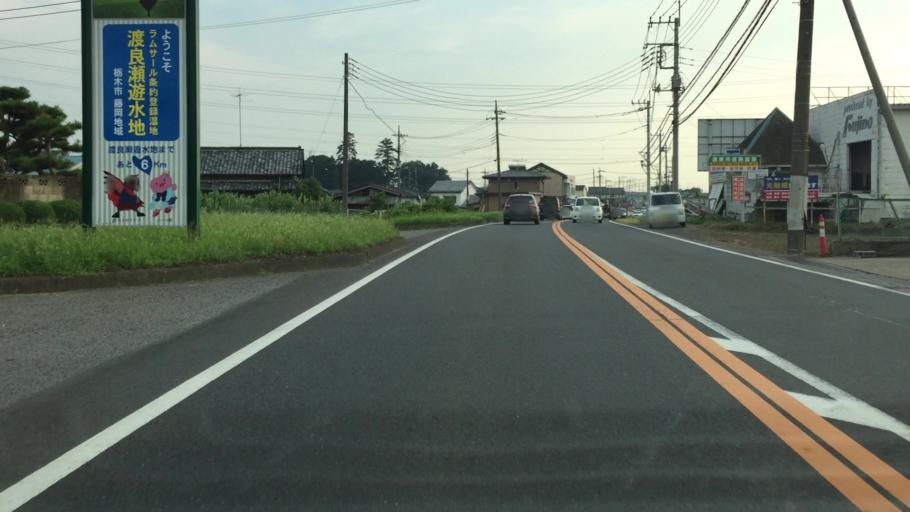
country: JP
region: Tochigi
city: Fujioka
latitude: 36.2820
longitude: 139.6637
